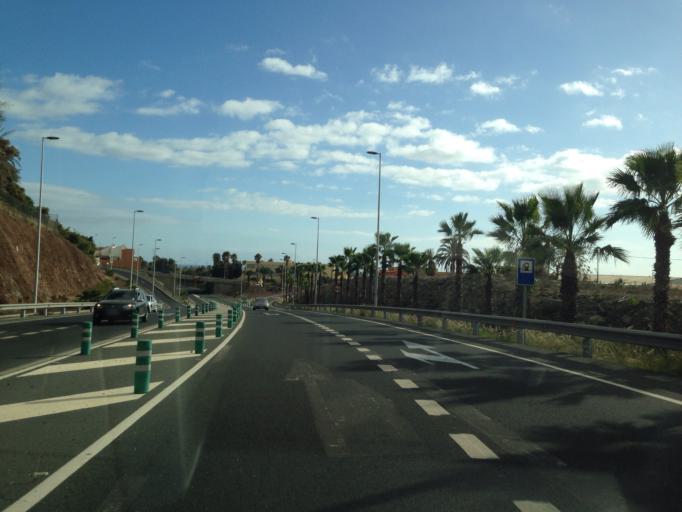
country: ES
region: Canary Islands
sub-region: Provincia de Las Palmas
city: Maspalomas
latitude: 27.7693
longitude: -15.5911
